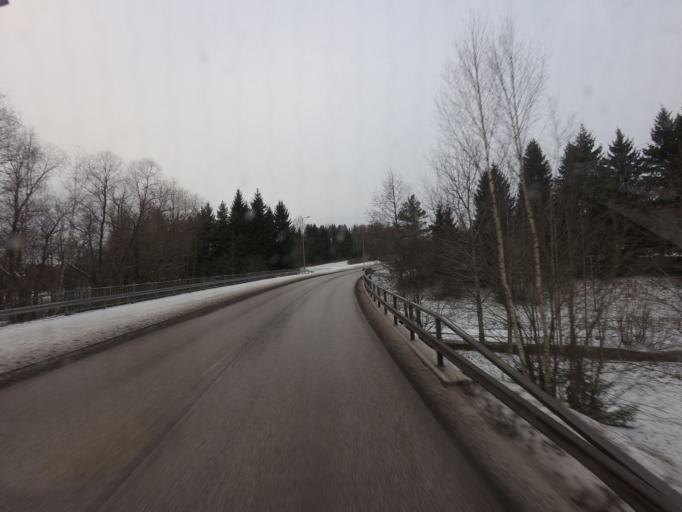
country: FI
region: Uusimaa
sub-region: Helsinki
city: Espoo
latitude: 60.2047
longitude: 24.6440
